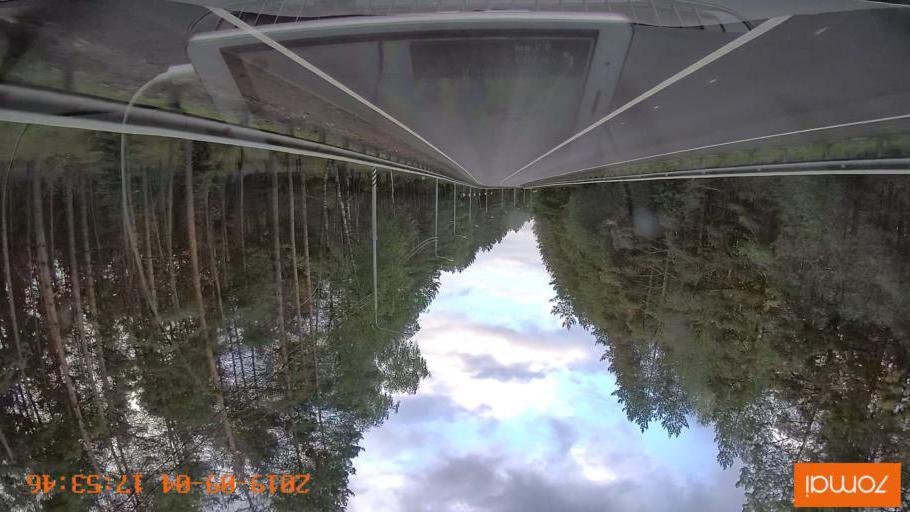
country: RU
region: Moskovskaya
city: Imeni Tsyurupy
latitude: 55.5144
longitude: 38.7284
